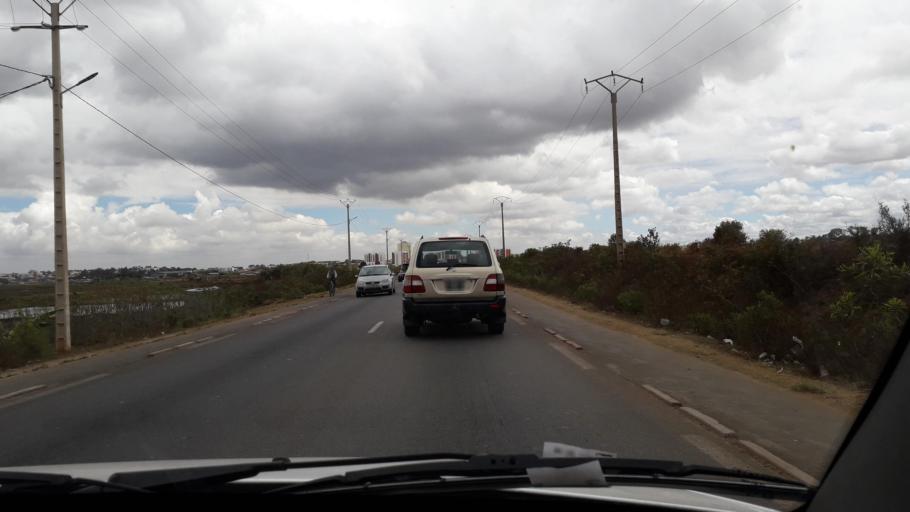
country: MG
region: Analamanga
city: Antananarivo
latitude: -18.8082
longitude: 47.5039
